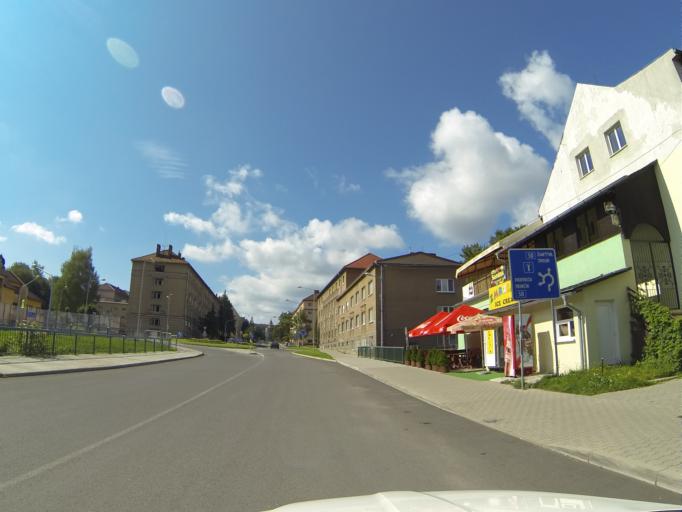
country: SK
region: Nitriansky
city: Handlova
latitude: 48.7268
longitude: 18.7596
